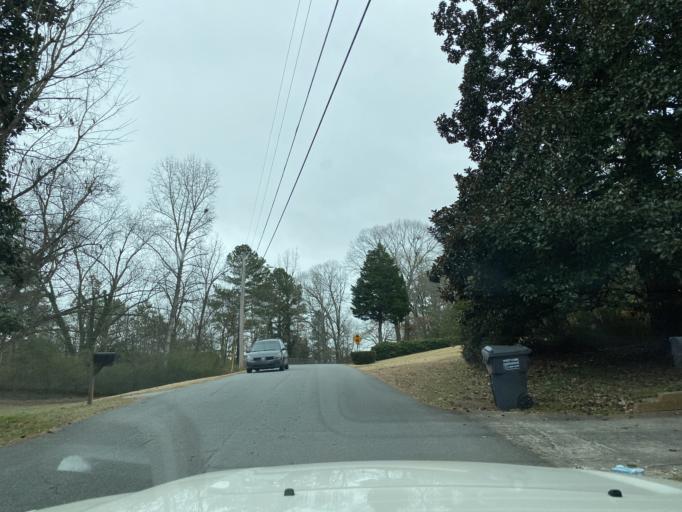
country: US
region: Georgia
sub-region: Cobb County
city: Fair Oaks
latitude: 33.9205
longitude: -84.5827
